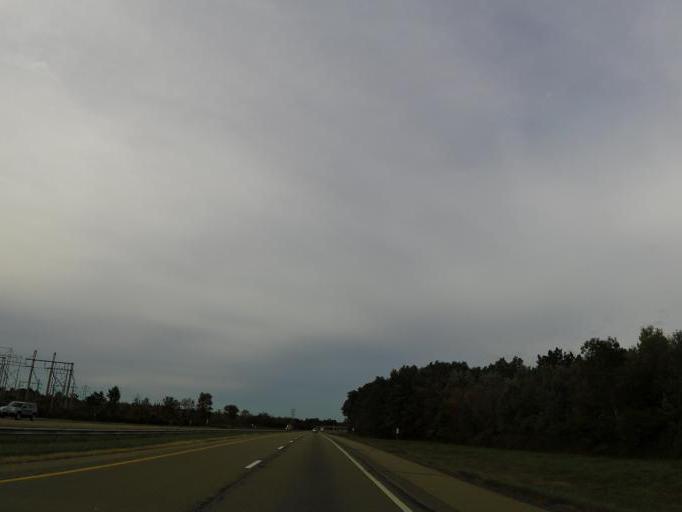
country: US
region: New York
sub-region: Chautauqua County
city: Dunkirk
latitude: 42.4833
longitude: -79.2583
